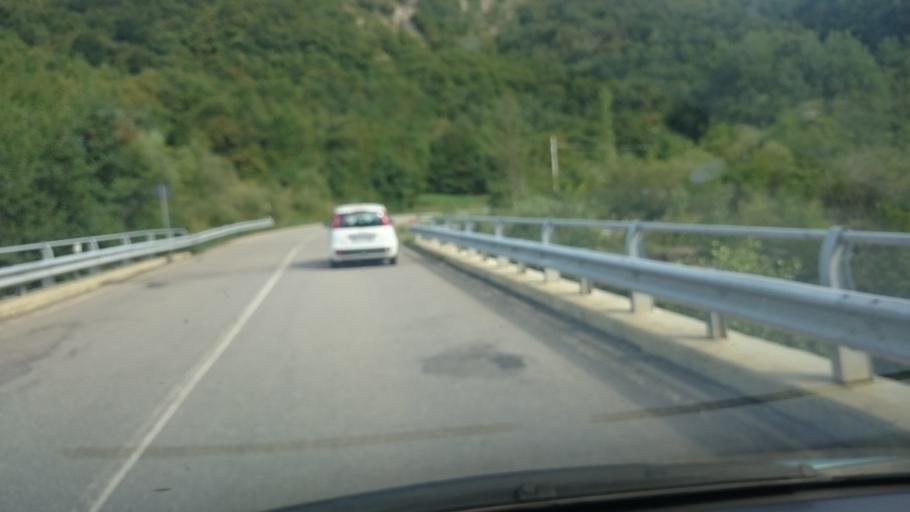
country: IT
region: Emilia-Romagna
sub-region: Provincia di Reggio Emilia
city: Villa Minozzo
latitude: 44.3166
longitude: 10.4633
